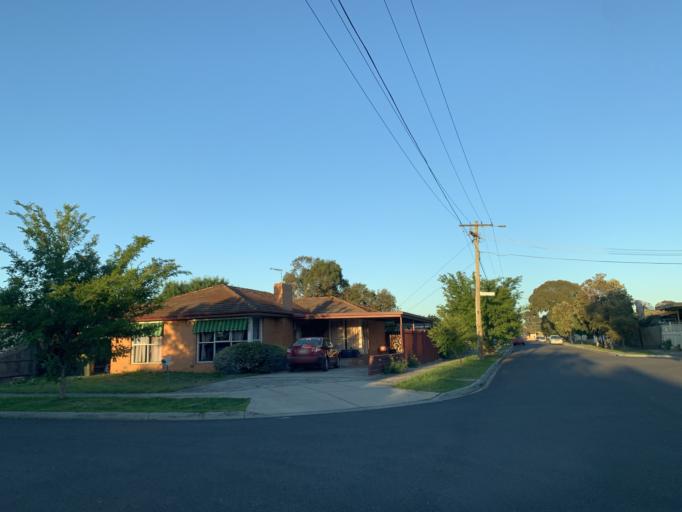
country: AU
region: Victoria
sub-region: Brimbank
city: St Albans
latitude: -37.7491
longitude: 144.8144
